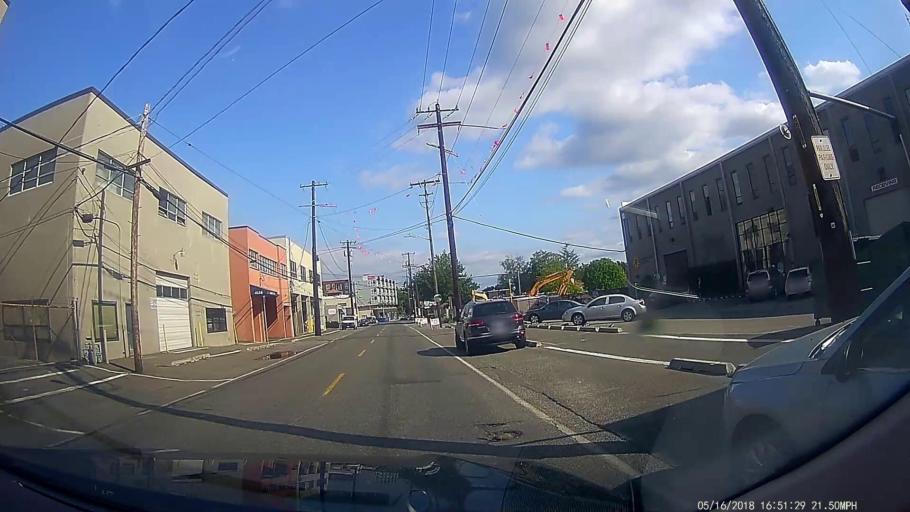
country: US
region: Washington
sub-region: King County
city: Seattle
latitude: 47.6631
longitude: -122.2949
